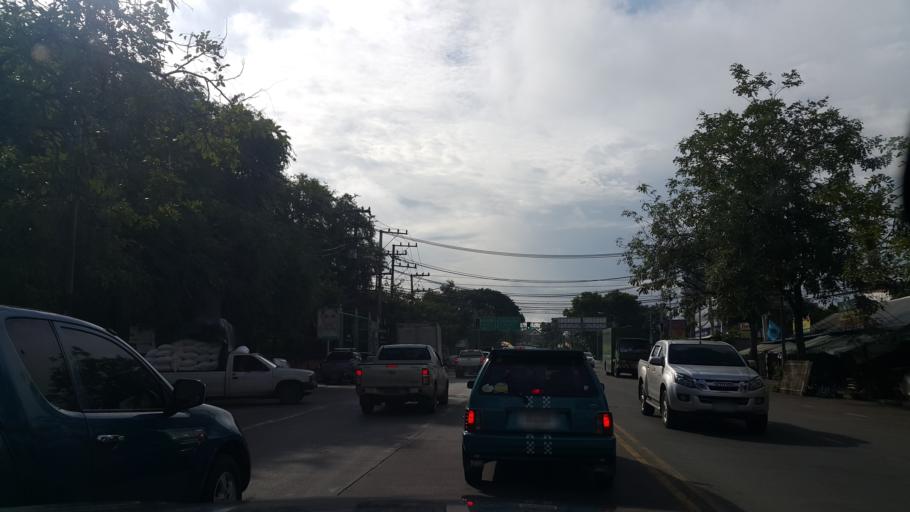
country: TH
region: Chiang Mai
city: Chiang Mai
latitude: 18.8010
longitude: 99.0012
